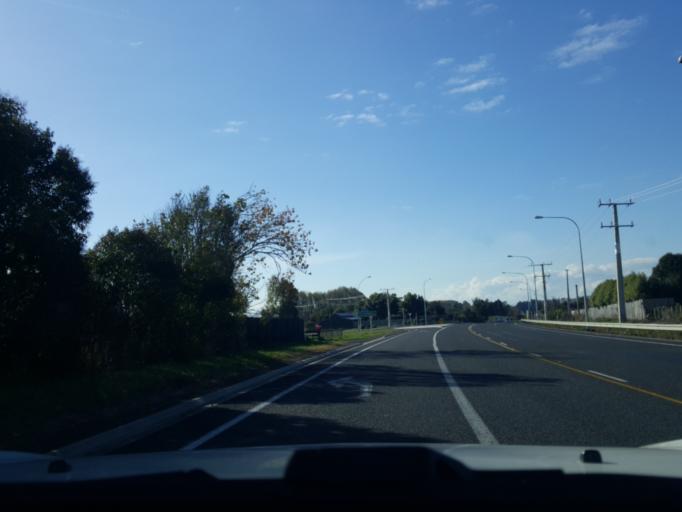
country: NZ
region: Waikato
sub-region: Waikato District
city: Ngaruawahia
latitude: -37.7549
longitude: 175.1525
